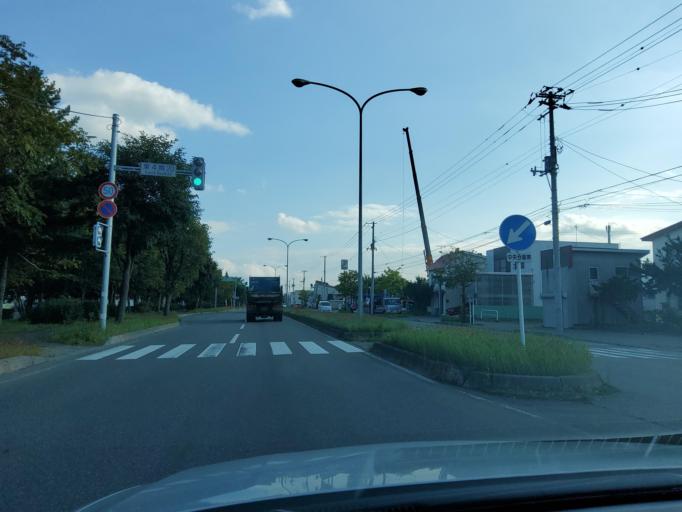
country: JP
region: Hokkaido
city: Obihiro
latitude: 42.9103
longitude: 143.2134
